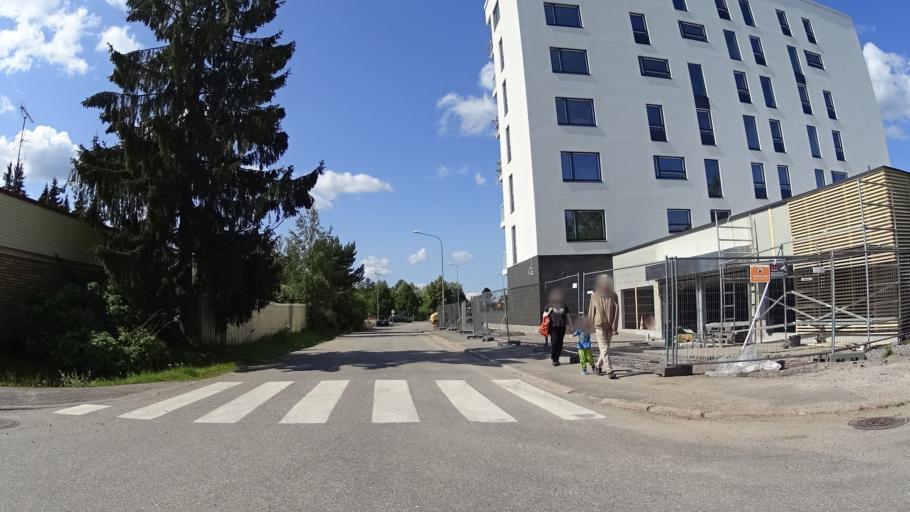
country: FI
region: Uusimaa
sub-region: Helsinki
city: Jaervenpaeae
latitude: 60.4656
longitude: 25.0880
